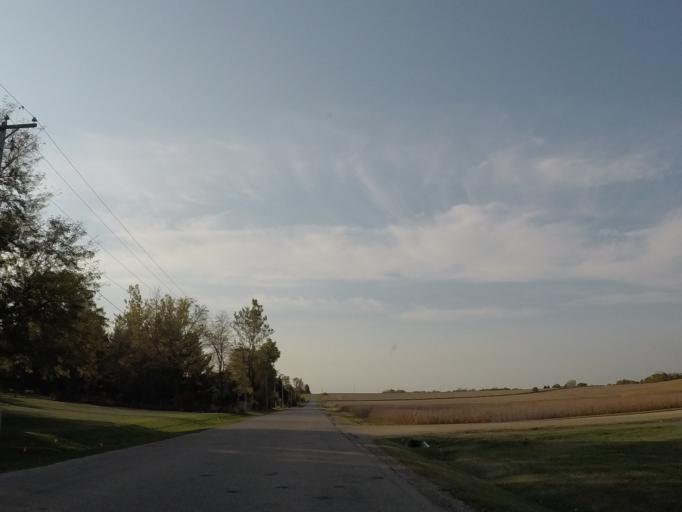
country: US
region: Wisconsin
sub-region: Dane County
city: Cross Plains
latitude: 43.0587
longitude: -89.6010
